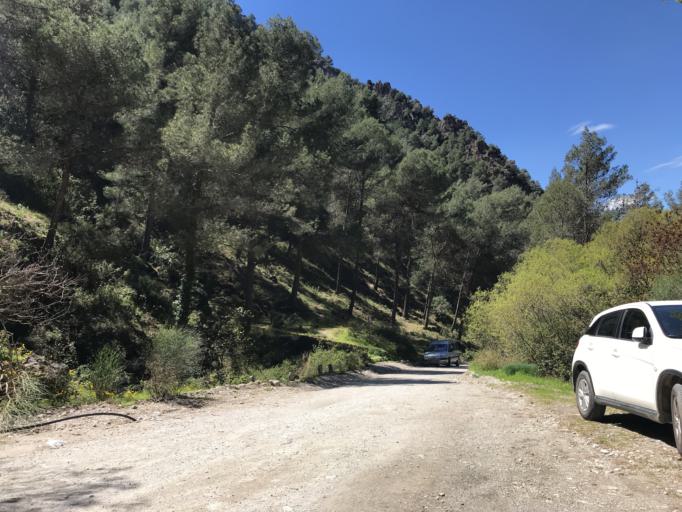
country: ES
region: Andalusia
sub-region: Provincia de Malaga
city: Alcaucin
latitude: 36.9151
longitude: -4.0910
